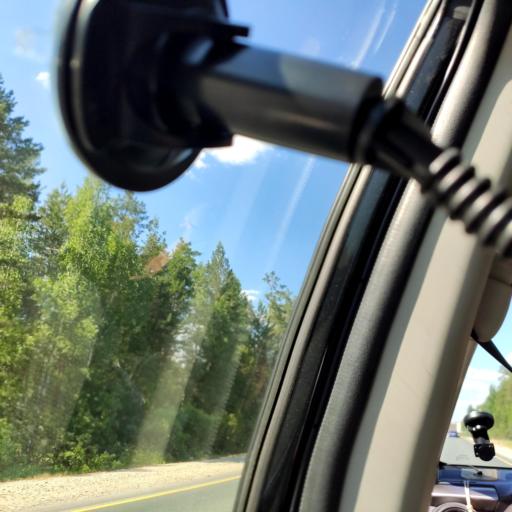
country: RU
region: Mariy-El
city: Suslonger
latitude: 56.2491
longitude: 48.2323
